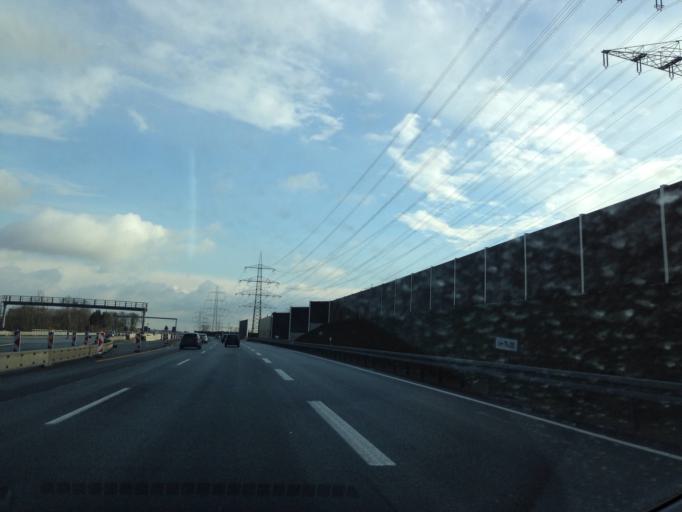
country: DE
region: North Rhine-Westphalia
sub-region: Regierungsbezirk Dusseldorf
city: Kaarst
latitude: 51.2217
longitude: 6.6399
